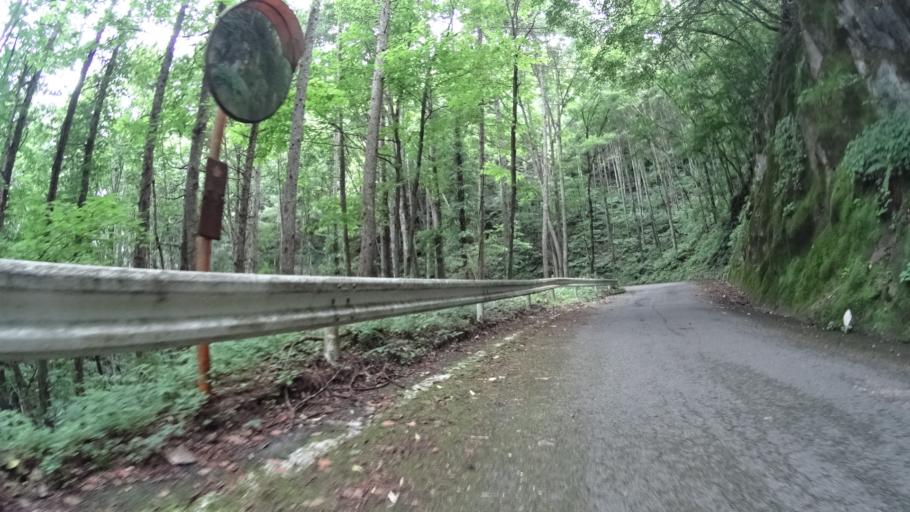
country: JP
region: Nagano
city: Saku
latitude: 36.0720
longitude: 138.6448
